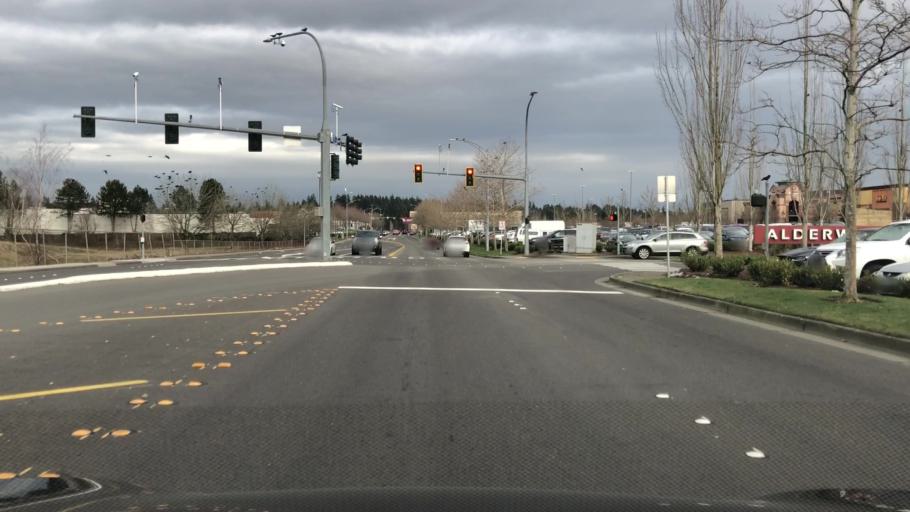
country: US
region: Washington
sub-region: Snohomish County
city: Alderwood Manor
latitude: 47.8318
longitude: -122.2739
